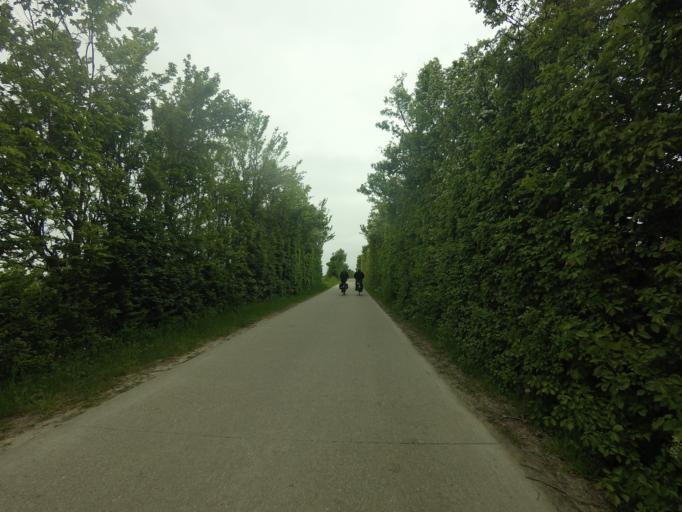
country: NL
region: Zeeland
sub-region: Gemeente Middelburg
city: Middelburg
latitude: 51.5467
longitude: 3.5759
